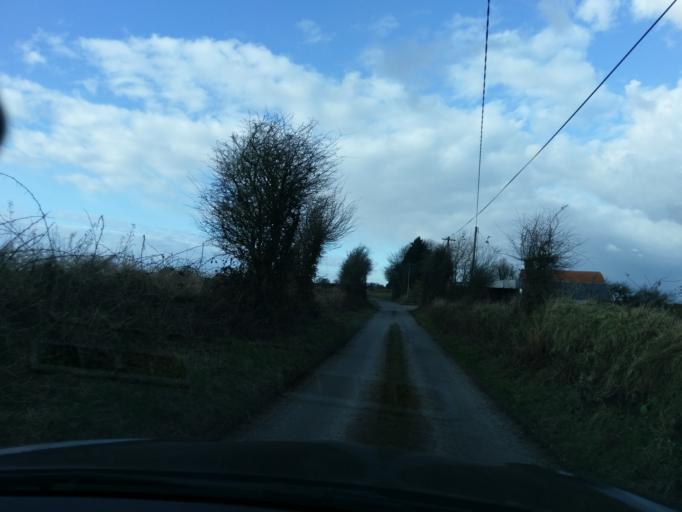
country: IE
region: Connaught
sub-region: County Galway
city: Athenry
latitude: 53.4576
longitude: -8.6435
